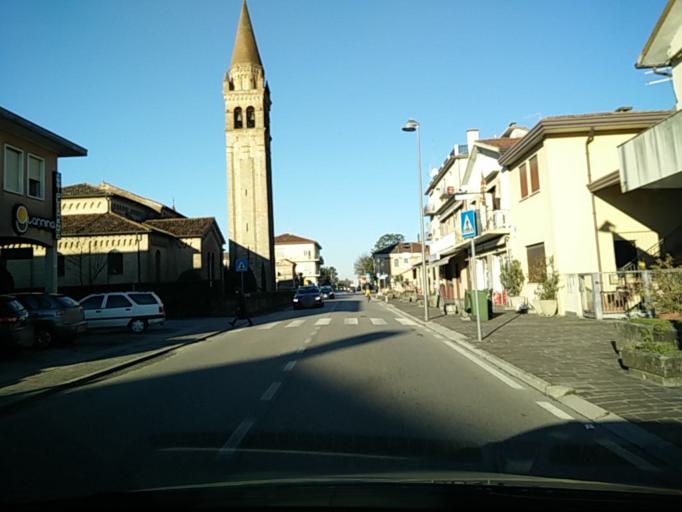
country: IT
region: Veneto
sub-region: Provincia di Venezia
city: Pianiga
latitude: 45.4559
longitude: 12.0315
